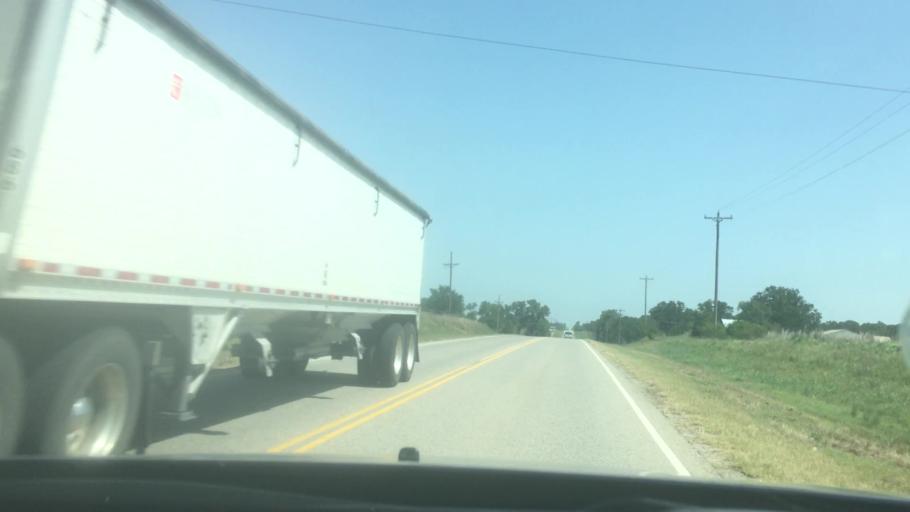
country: US
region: Oklahoma
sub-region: Bryan County
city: Durant
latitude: 34.2389
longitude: -96.4248
